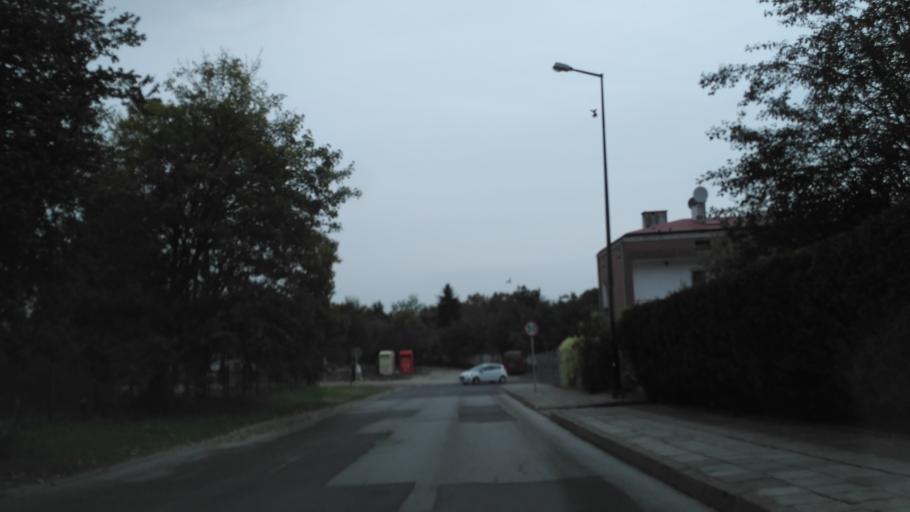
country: PL
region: Lublin Voivodeship
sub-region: Powiat lubelski
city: Lublin
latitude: 51.2260
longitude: 22.5938
